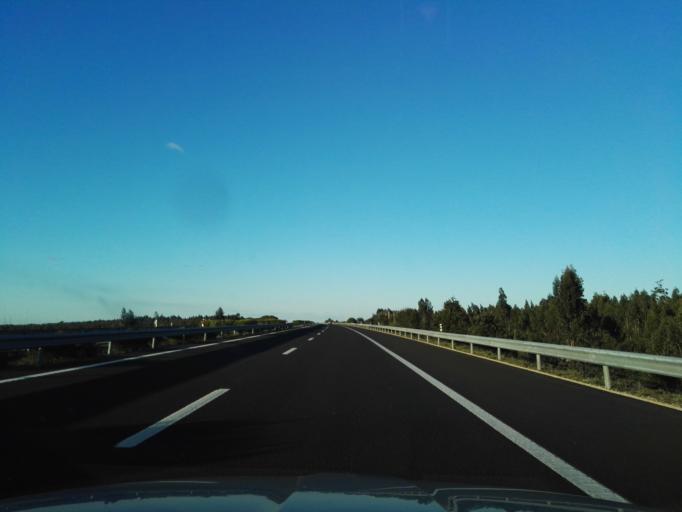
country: PT
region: Santarem
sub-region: Benavente
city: Poceirao
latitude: 38.7628
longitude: -8.6833
